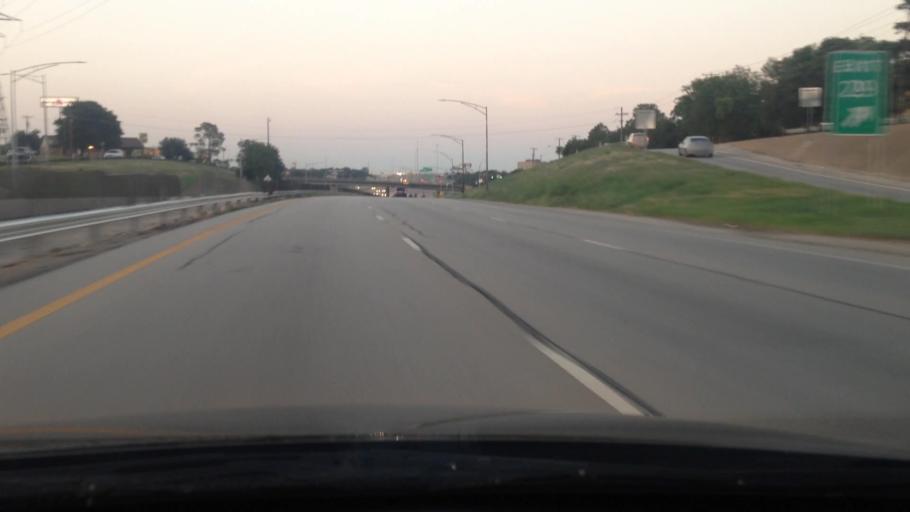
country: US
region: Texas
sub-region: Tarrant County
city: Haltom City
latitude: 32.7432
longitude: -97.2240
